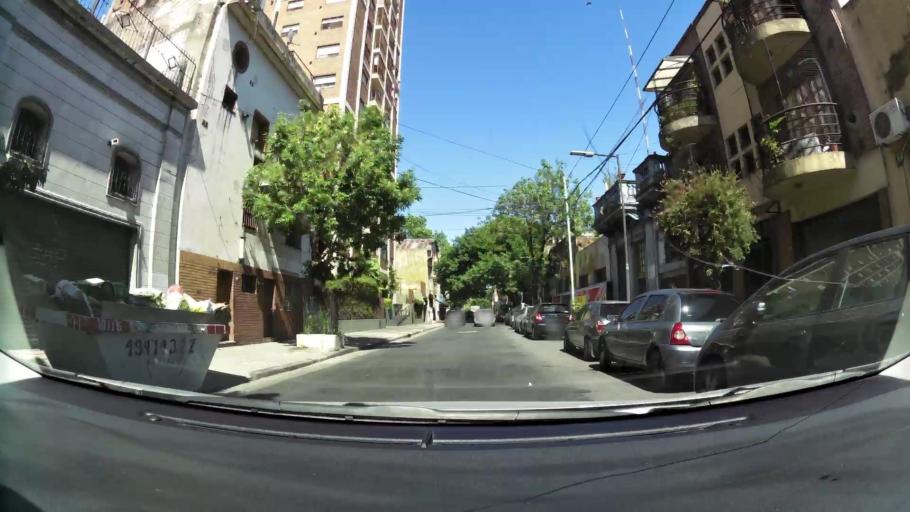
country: AR
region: Buenos Aires F.D.
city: Buenos Aires
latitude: -34.6315
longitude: -58.3895
